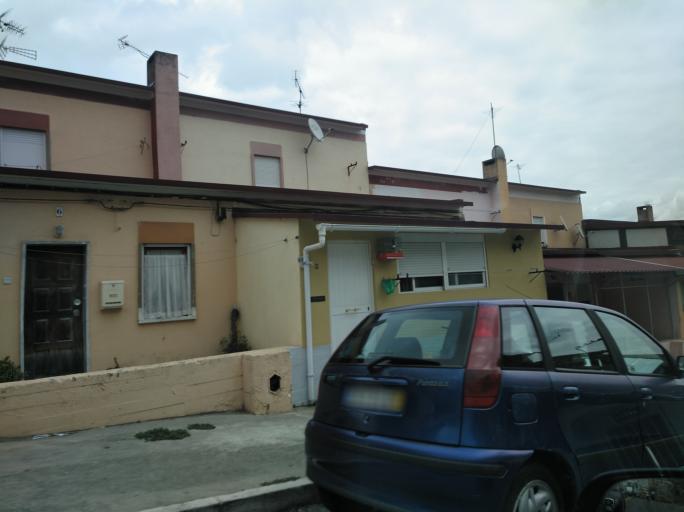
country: PT
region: Lisbon
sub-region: Lisbon
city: Lisbon
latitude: 38.7357
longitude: -9.1193
